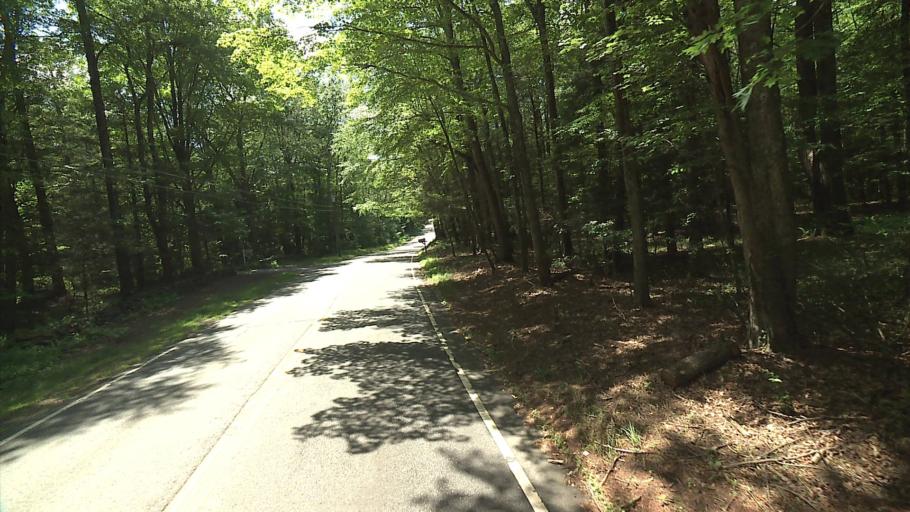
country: US
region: Connecticut
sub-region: Windham County
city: South Woodstock
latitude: 41.9768
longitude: -72.0373
